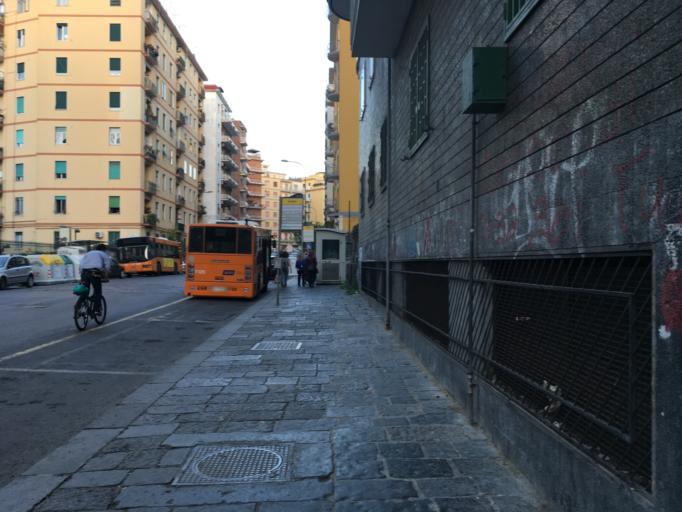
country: IT
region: Campania
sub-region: Provincia di Napoli
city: Napoli
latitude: 40.8507
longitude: 14.2343
